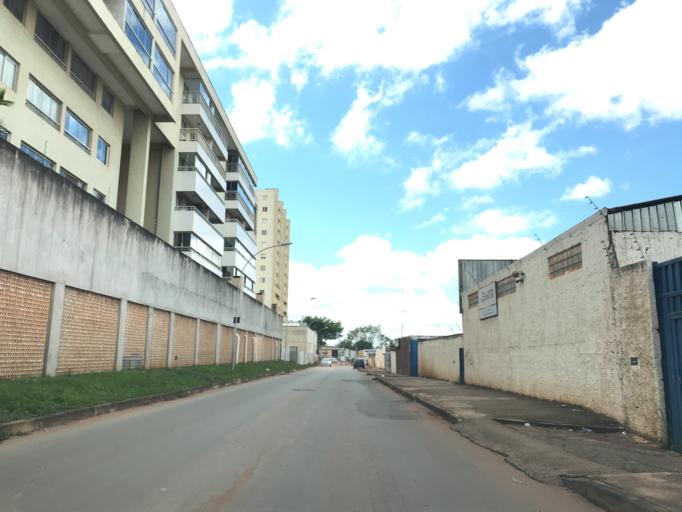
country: BR
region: Federal District
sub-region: Brasilia
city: Brasilia
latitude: -15.8317
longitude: -47.9883
